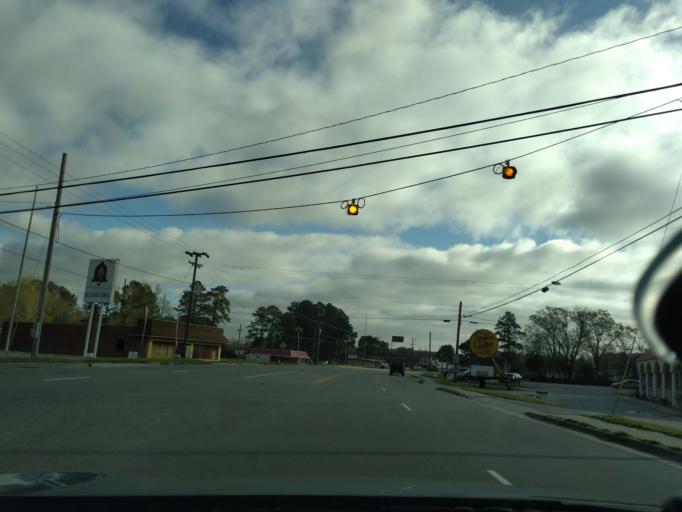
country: US
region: North Carolina
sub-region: Washington County
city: Plymouth
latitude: 35.8568
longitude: -76.7483
